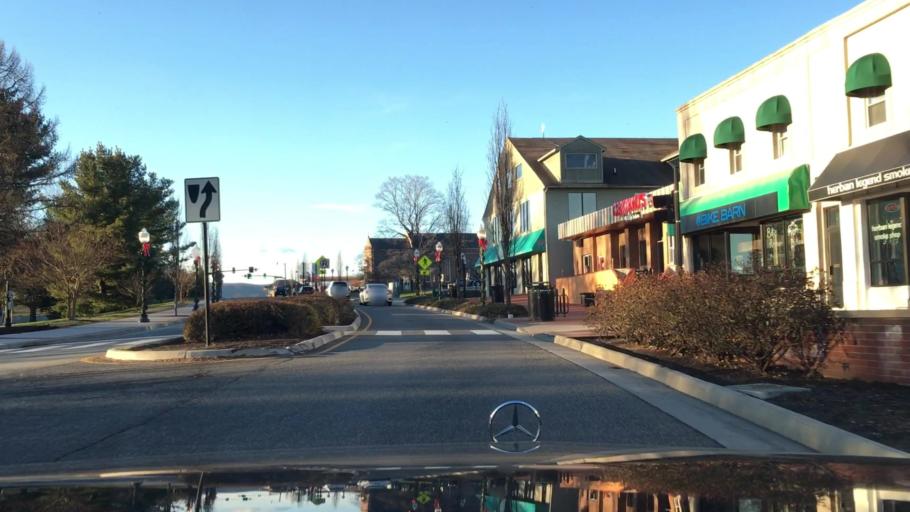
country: US
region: Virginia
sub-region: Montgomery County
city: Blacksburg
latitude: 37.2316
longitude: -80.4161
